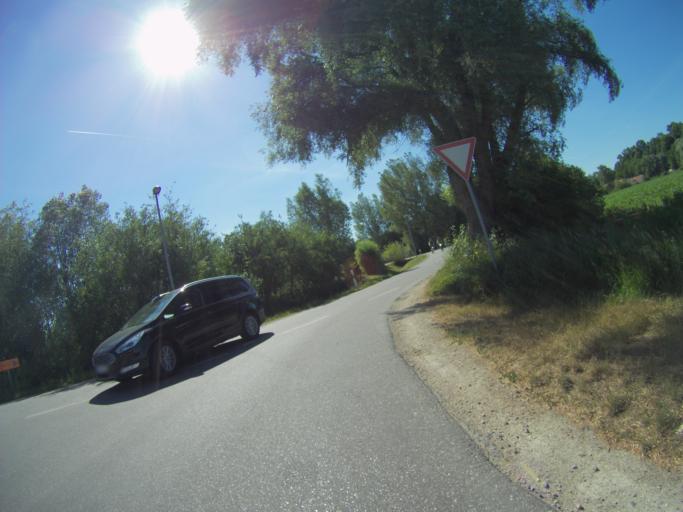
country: DE
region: Bavaria
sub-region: Upper Bavaria
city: Freising
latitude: 48.3911
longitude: 11.7266
